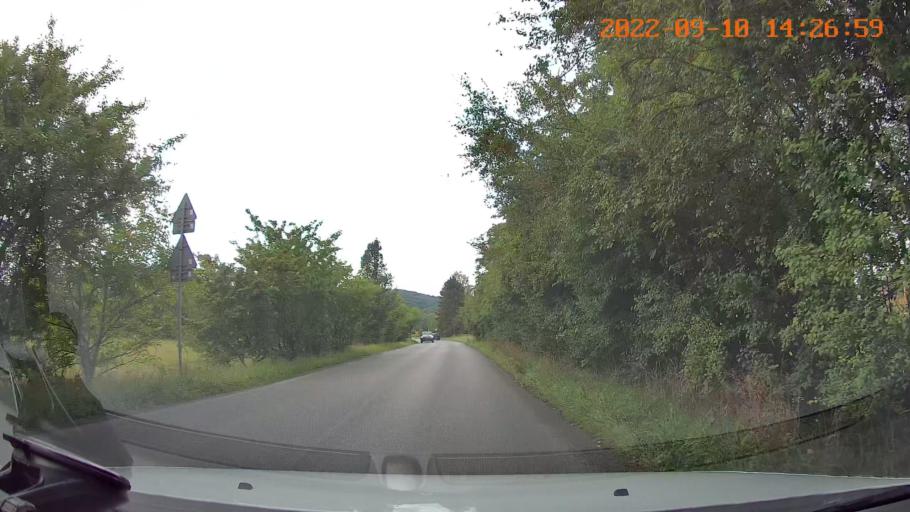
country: PL
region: Lesser Poland Voivodeship
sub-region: Powiat krakowski
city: Rzaska
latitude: 50.0770
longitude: 19.8494
